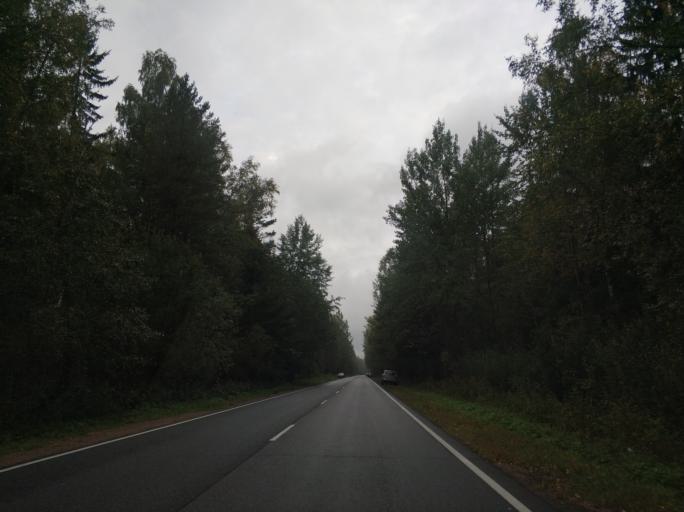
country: RU
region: Leningrad
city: Borisova Griva
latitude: 60.1550
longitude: 30.9311
